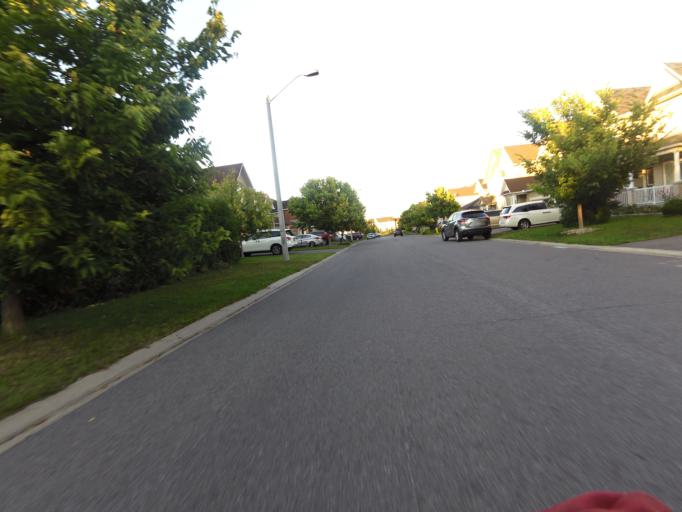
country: CA
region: Ontario
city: Bells Corners
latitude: 45.3479
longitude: -75.9469
